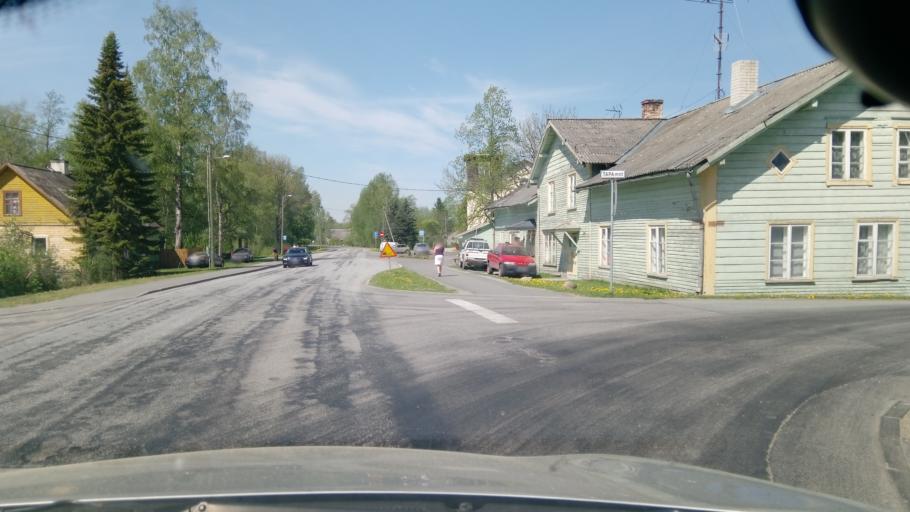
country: EE
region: Laeaene-Virumaa
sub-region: Tapa vald
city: Tapa
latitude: 59.1922
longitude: 25.8392
